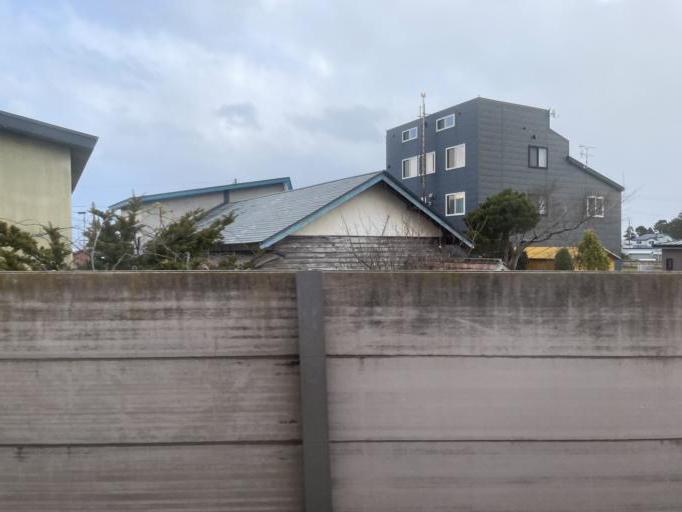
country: JP
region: Aomori
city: Aomori Shi
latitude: 41.0179
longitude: 140.6465
